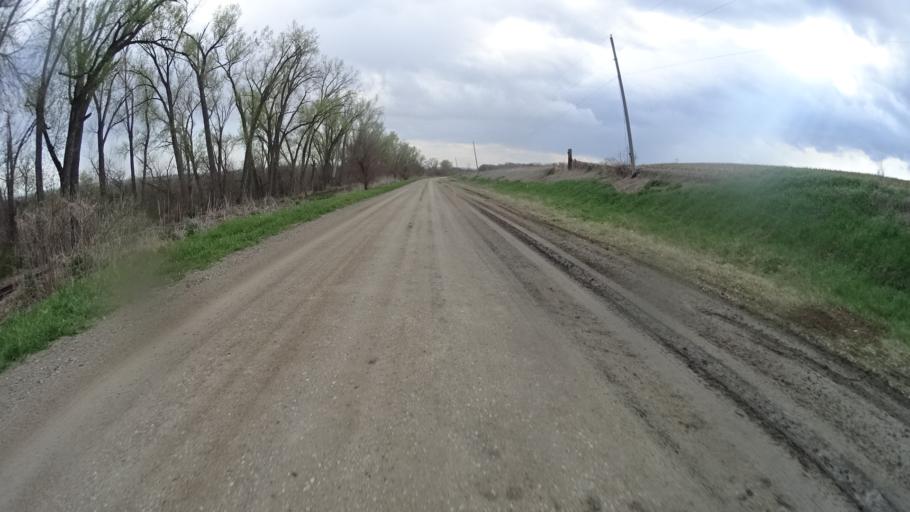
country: US
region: Nebraska
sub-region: Sarpy County
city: Offutt Air Force Base
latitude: 41.0956
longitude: -95.9135
